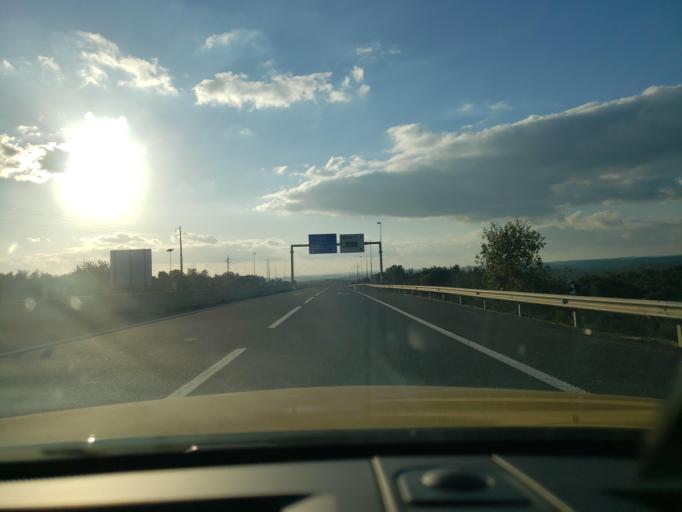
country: PT
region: Faro
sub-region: Portimao
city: Portimao
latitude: 37.1773
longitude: -8.5611
